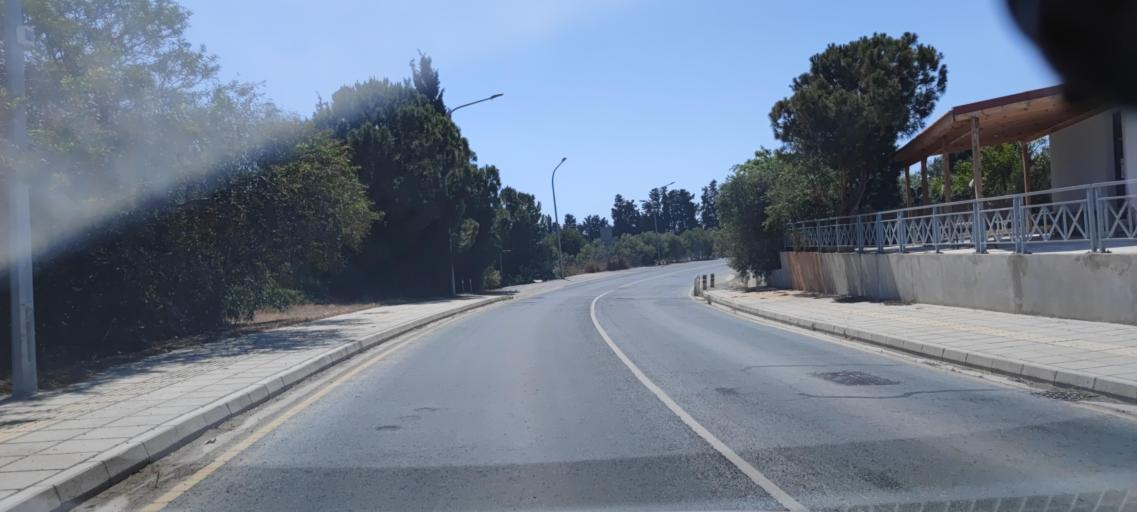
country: CY
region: Larnaka
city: Kolossi
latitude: 34.6536
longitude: 32.9569
